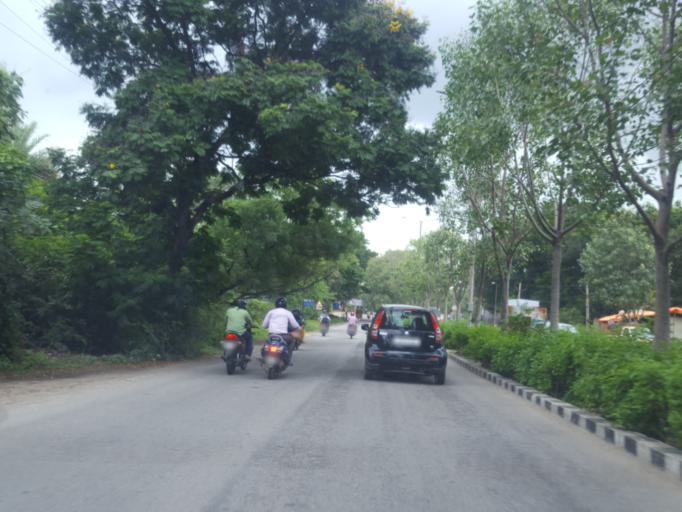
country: IN
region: Telangana
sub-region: Medak
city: Serilingampalle
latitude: 17.4608
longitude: 78.3368
